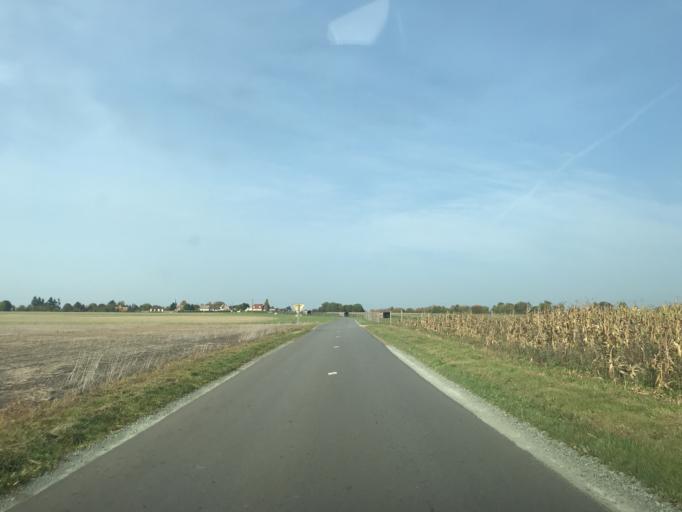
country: FR
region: Haute-Normandie
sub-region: Departement de l'Eure
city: La Chapelle-Reanville
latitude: 49.0665
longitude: 1.4086
